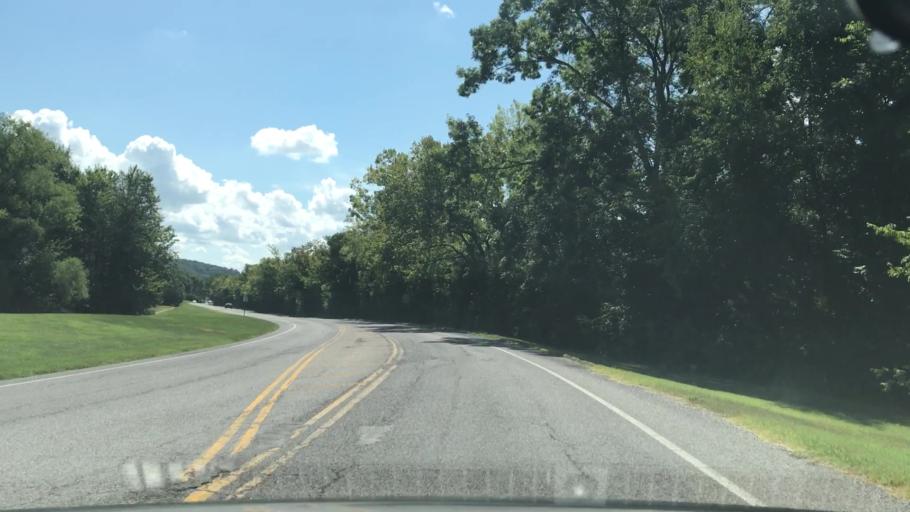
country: US
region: Tennessee
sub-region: Williamson County
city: Franklin
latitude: 35.9784
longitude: -86.8859
